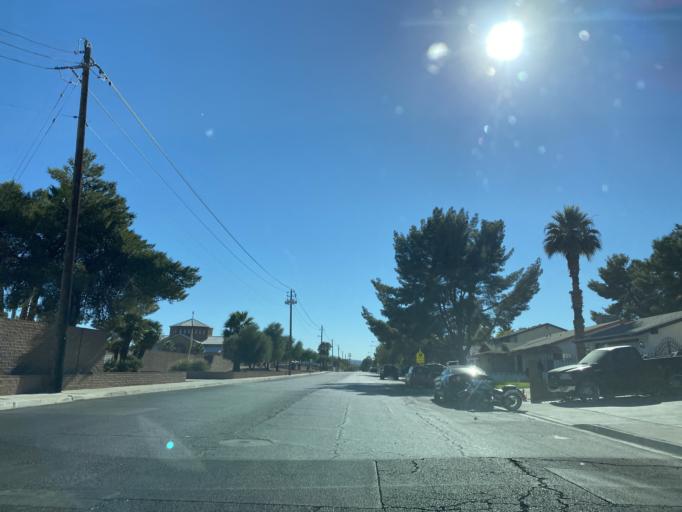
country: US
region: Nevada
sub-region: Clark County
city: Whitney
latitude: 36.0930
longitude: -115.0869
